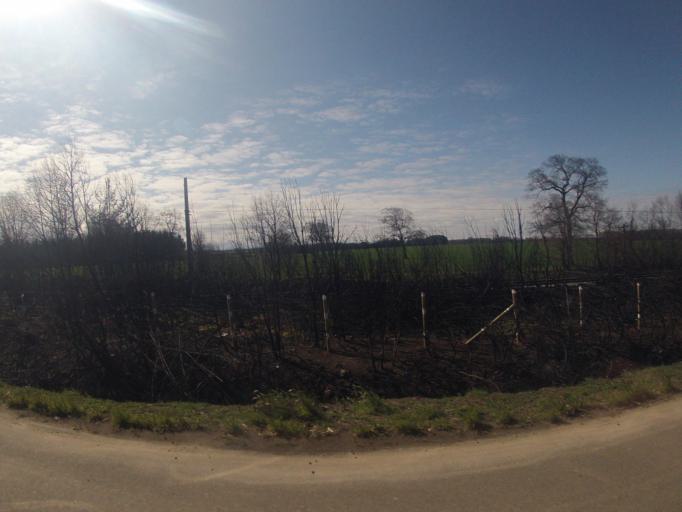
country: CL
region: Araucania
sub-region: Provincia de Malleco
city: Victoria
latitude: -38.1534
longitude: -72.3066
